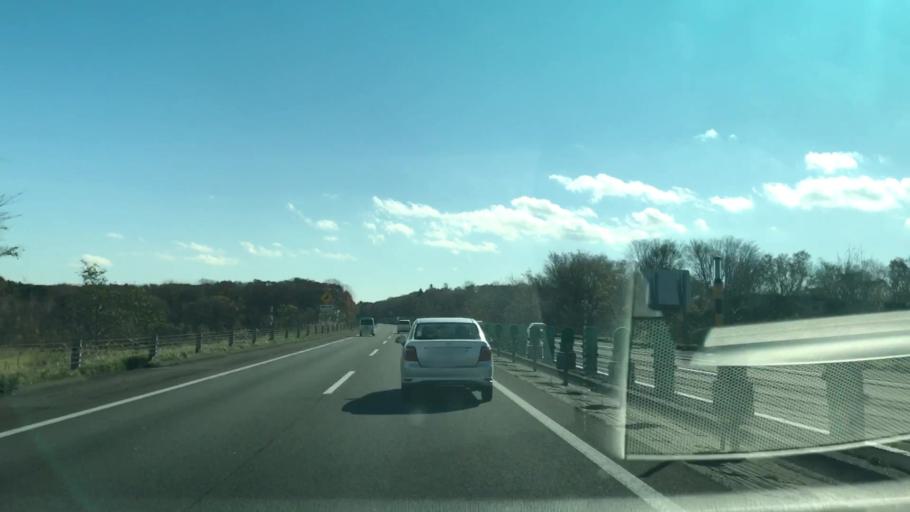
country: JP
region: Hokkaido
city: Chitose
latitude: 42.8648
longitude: 141.5574
